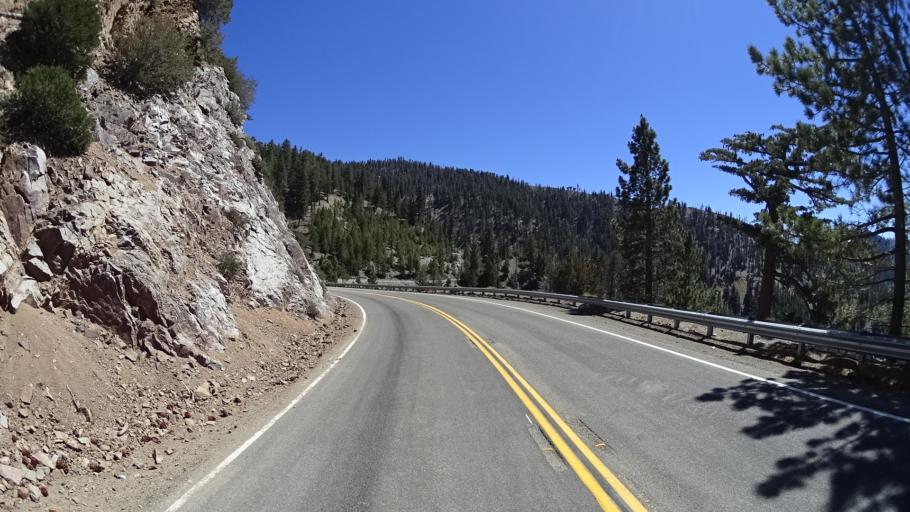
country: US
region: California
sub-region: San Bernardino County
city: Wrightwood
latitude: 34.3522
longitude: -117.8092
